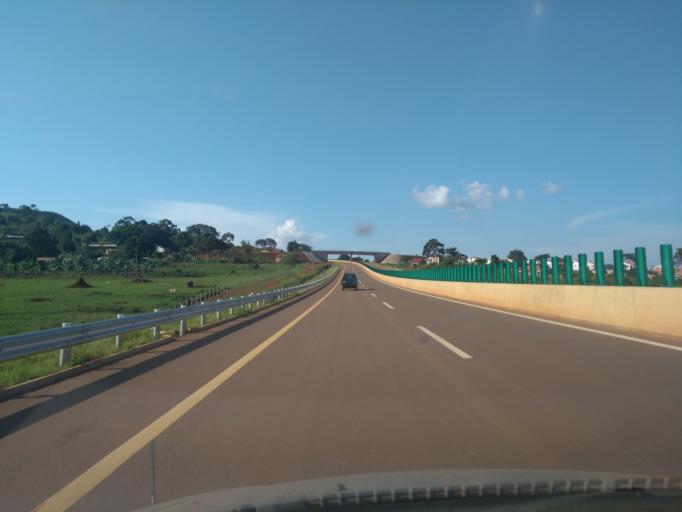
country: UG
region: Central Region
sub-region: Wakiso District
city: Kajansi
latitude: 0.1821
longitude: 32.5214
